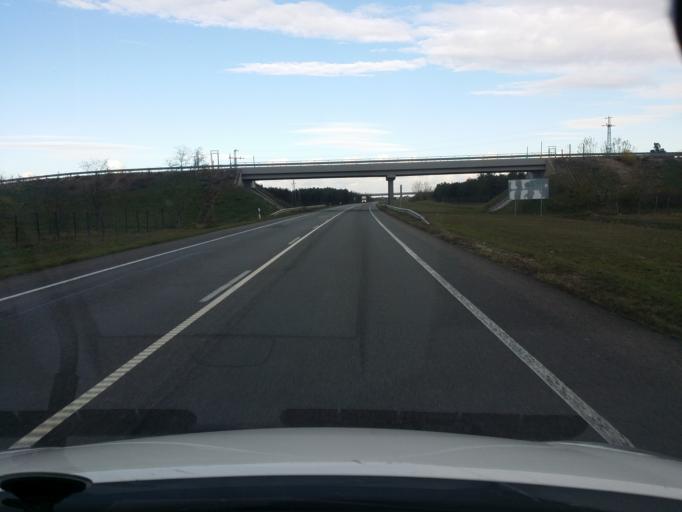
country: HU
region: Gyor-Moson-Sopron
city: Rajka
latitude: 47.9564
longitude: 17.1682
